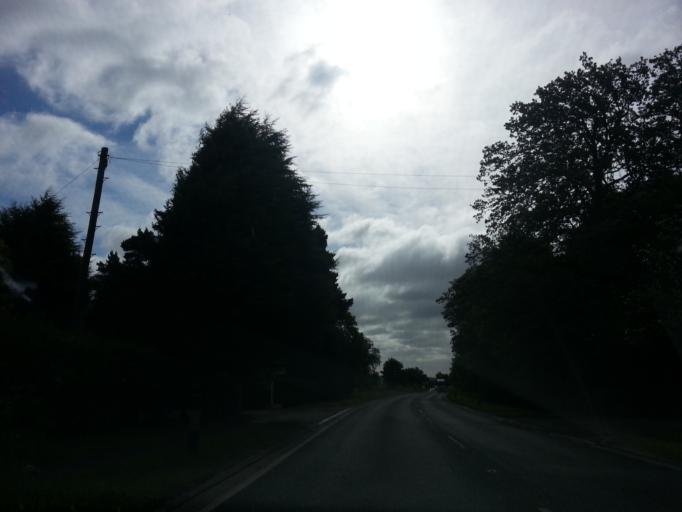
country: GB
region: England
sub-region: County Durham
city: Newton Aycliffe
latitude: 54.6544
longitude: -1.5820
